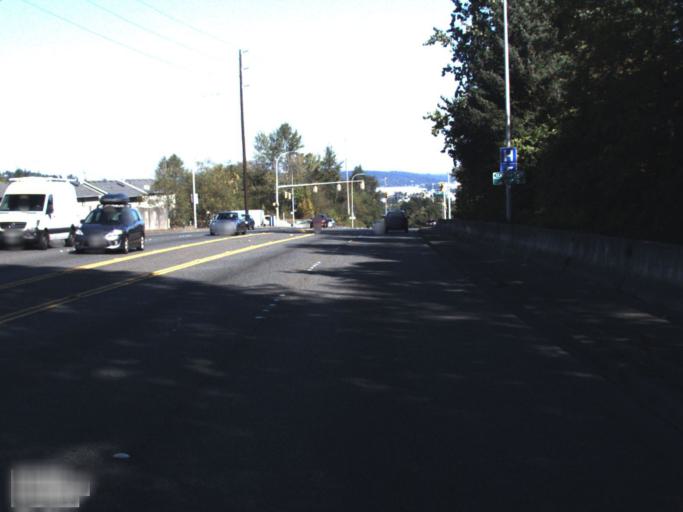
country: US
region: Washington
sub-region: King County
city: Renton
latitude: 47.4597
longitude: -122.2071
